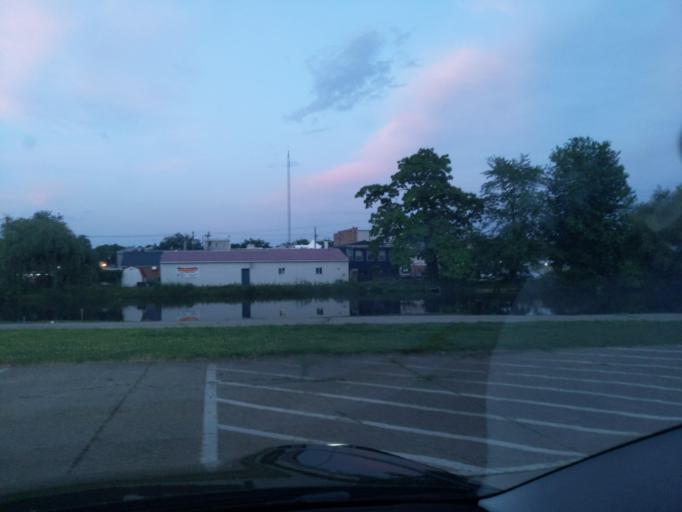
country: US
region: Michigan
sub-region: Eaton County
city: Eaton Rapids
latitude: 42.5125
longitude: -84.6583
